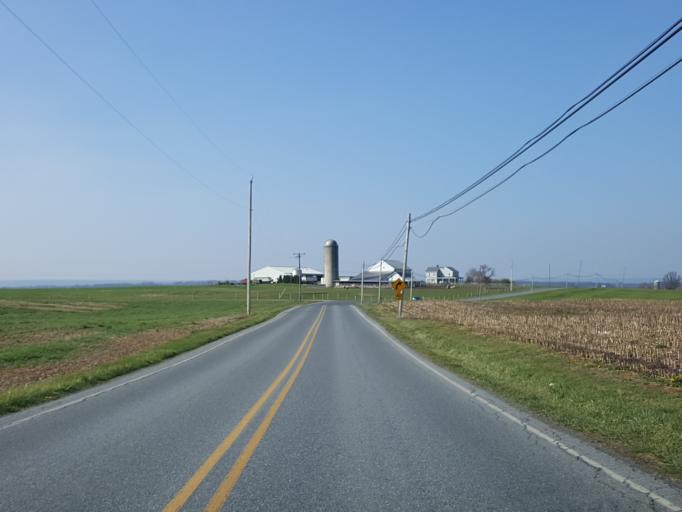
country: US
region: Pennsylvania
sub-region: Lebanon County
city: Annville
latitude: 40.2939
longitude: -76.5218
